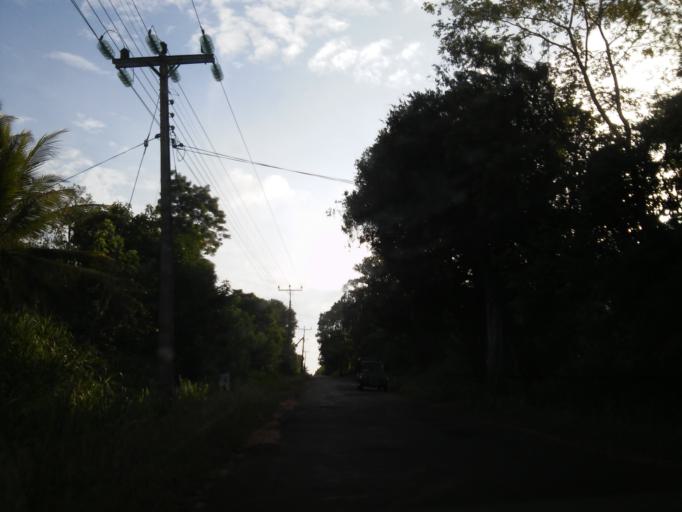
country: LK
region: Central
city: Sigiriya
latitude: 8.1394
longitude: 80.6380
